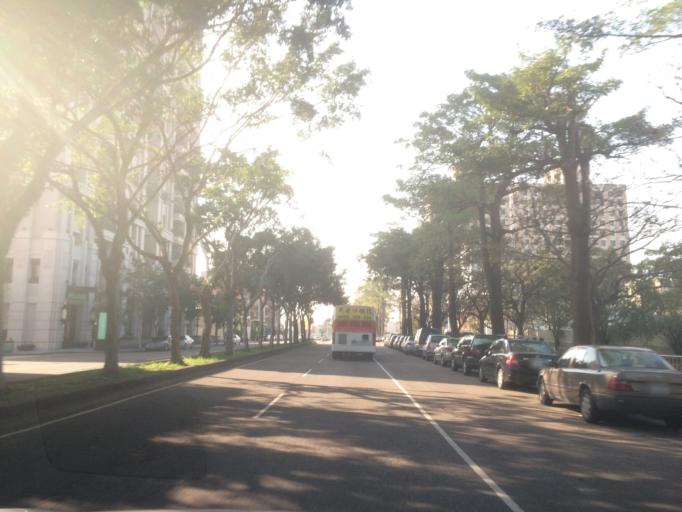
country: TW
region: Taiwan
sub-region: Taichung City
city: Taichung
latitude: 24.1817
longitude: 120.6846
